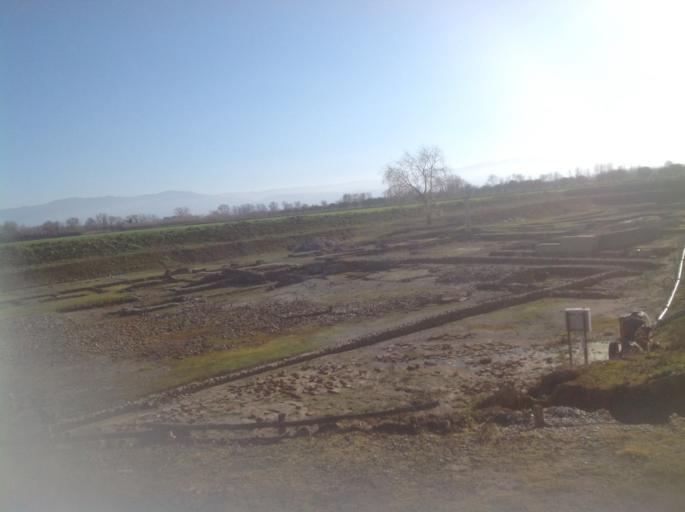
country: IT
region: Calabria
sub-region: Provincia di Cosenza
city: Sibari
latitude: 39.7188
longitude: 16.4976
